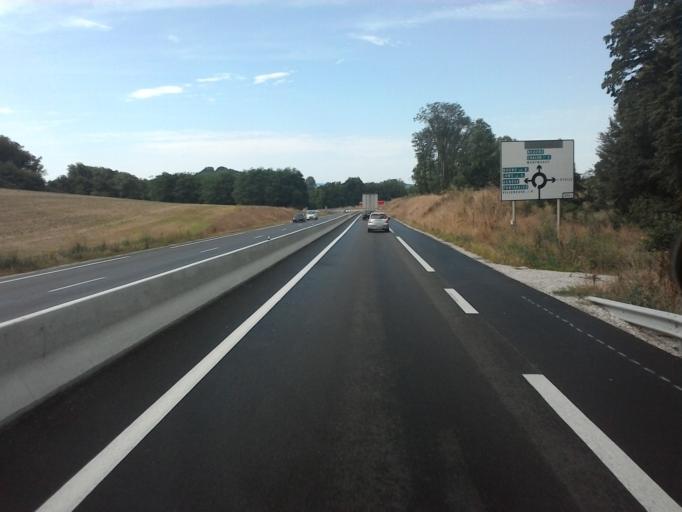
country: FR
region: Franche-Comte
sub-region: Departement du Jura
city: Lons-le-Saunier
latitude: 46.7100
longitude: 5.5510
